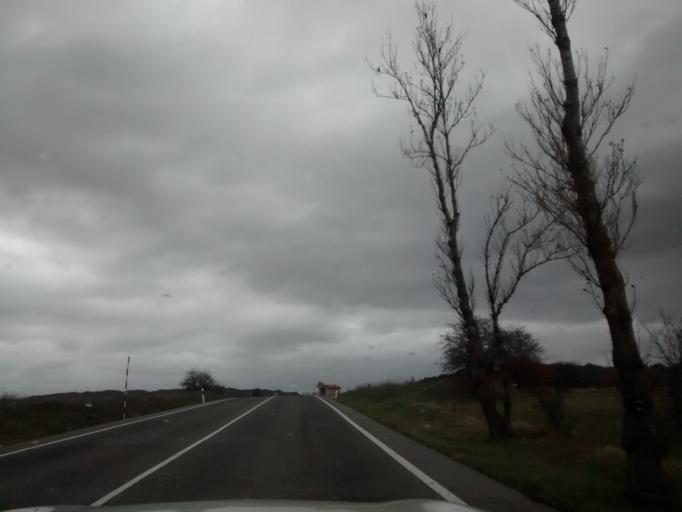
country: ES
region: Cantabria
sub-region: Provincia de Cantabria
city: San Pedro del Romeral
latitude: 42.9767
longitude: -3.8001
